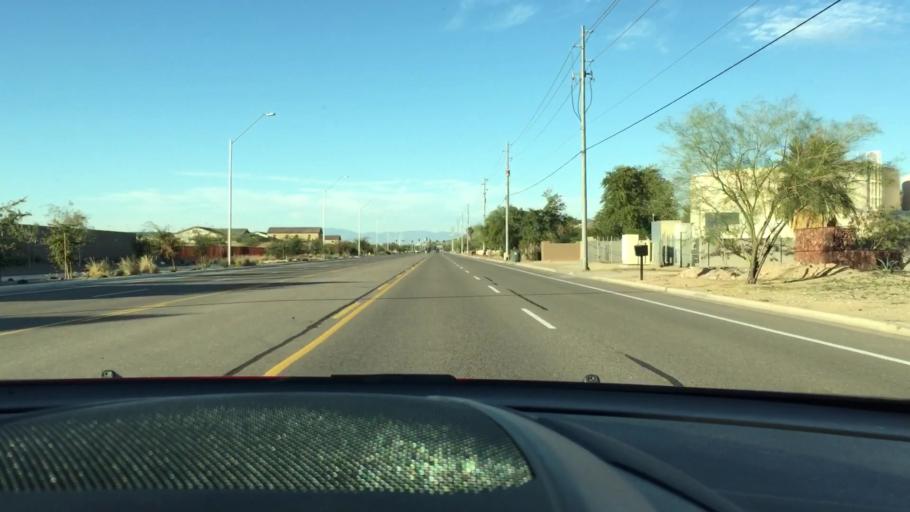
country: US
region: Arizona
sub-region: Maricopa County
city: Sun City
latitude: 33.6847
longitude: -112.2550
